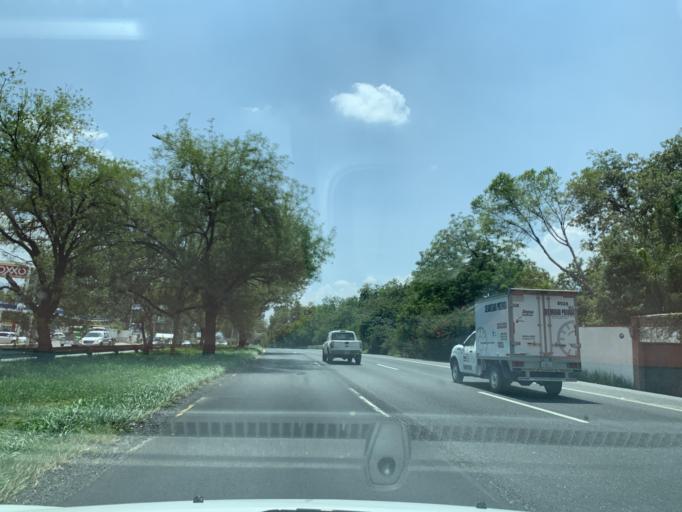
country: MX
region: Nuevo Leon
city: Santiago
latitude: 25.4713
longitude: -100.1760
